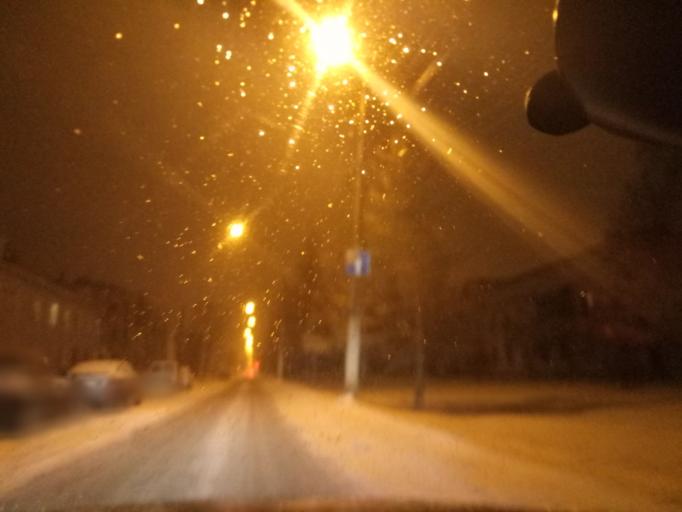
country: RU
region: Tula
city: Novomoskovsk
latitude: 54.0049
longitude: 38.2873
